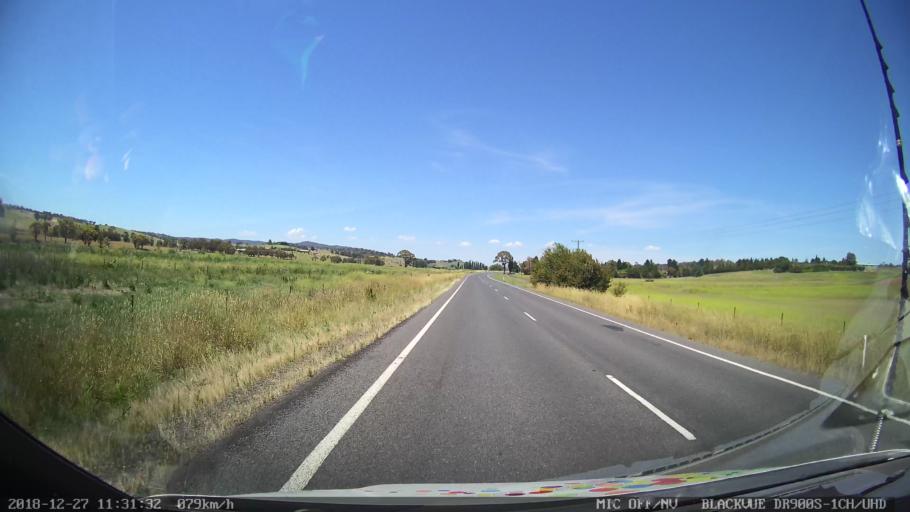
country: AU
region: New South Wales
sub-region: Bathurst Regional
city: Perthville
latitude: -33.4963
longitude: 149.5389
